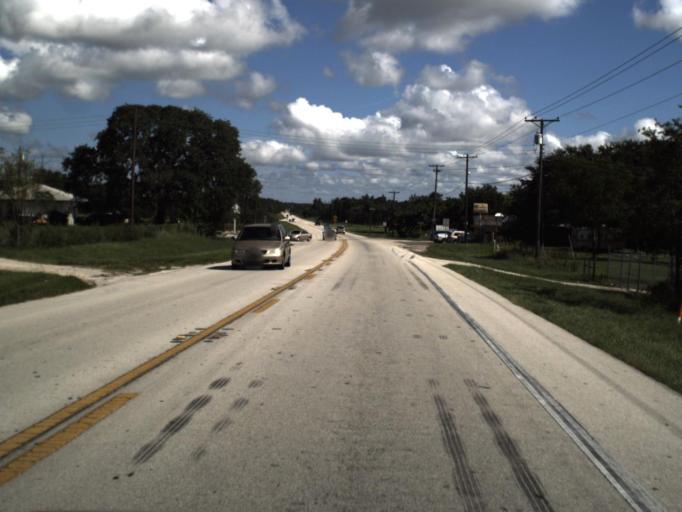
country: US
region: Florida
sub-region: Polk County
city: Haines City
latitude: 28.1310
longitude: -81.6141
